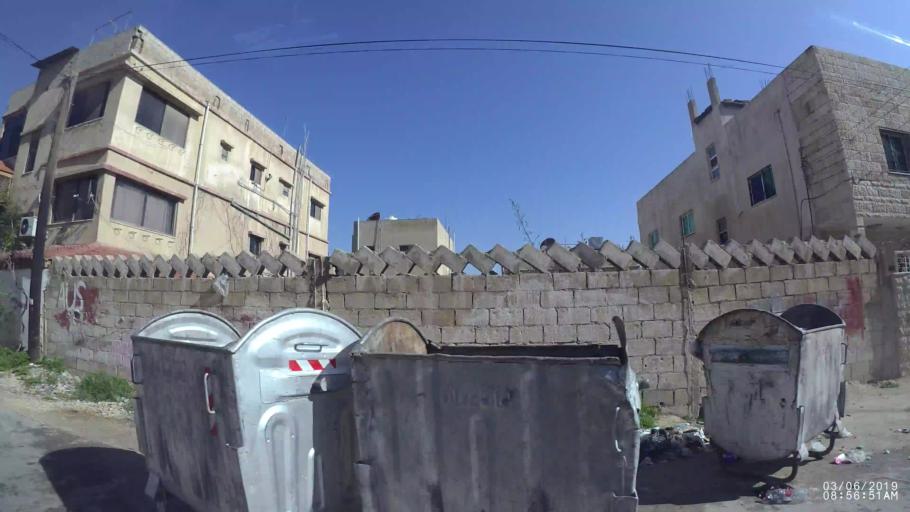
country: JO
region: Amman
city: Amman
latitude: 31.9906
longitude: 35.9913
